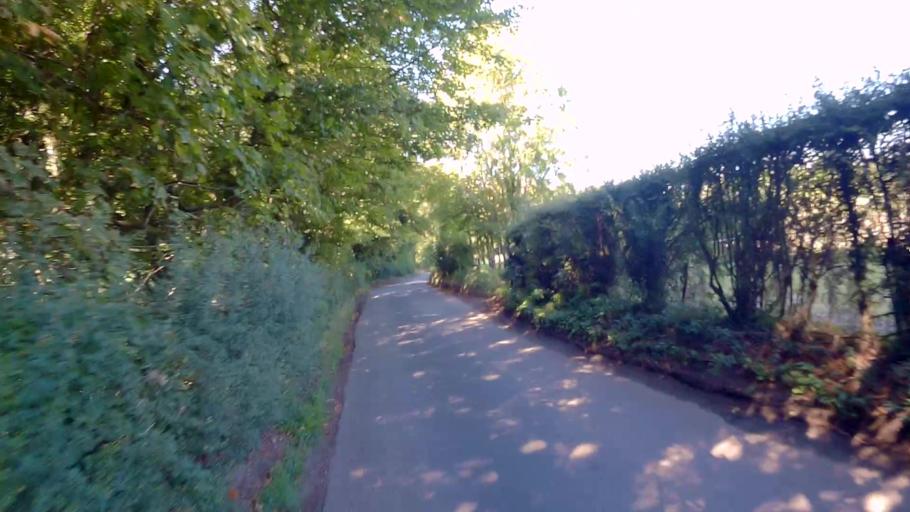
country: GB
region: England
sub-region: Hampshire
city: Overton
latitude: 51.2506
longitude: -1.1923
